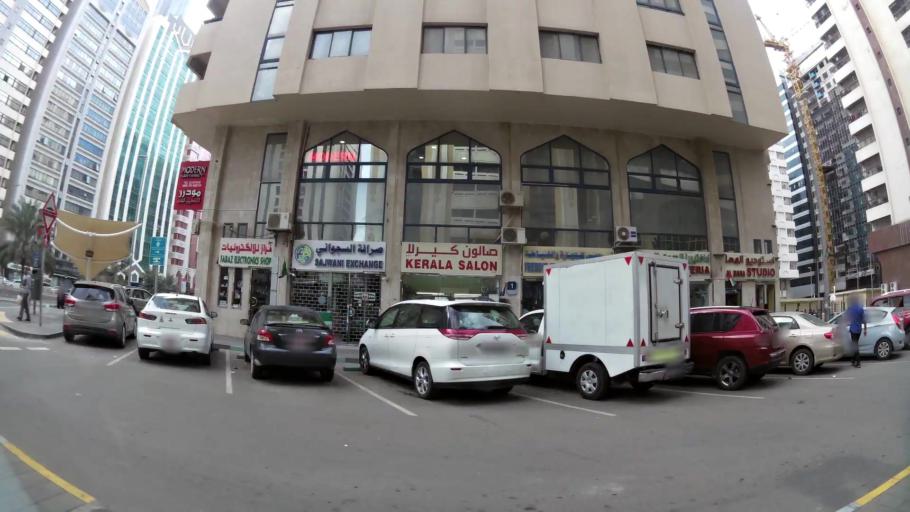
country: AE
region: Abu Dhabi
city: Abu Dhabi
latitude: 24.4883
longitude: 54.3601
